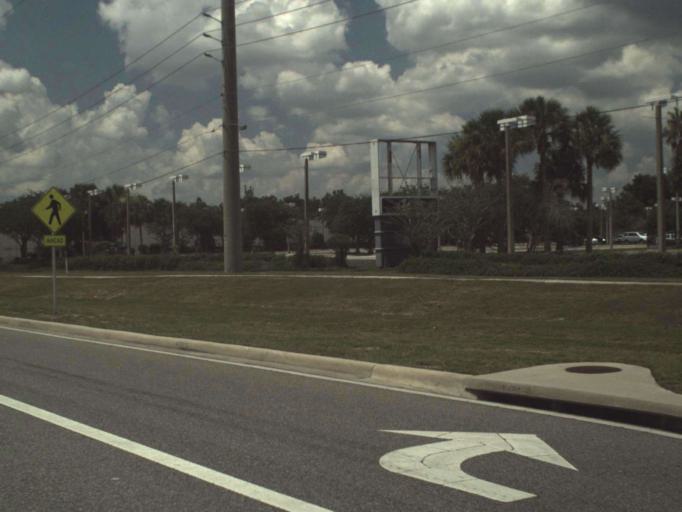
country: US
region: Florida
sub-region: Orange County
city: Lockhart
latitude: 28.6424
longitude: -81.4155
